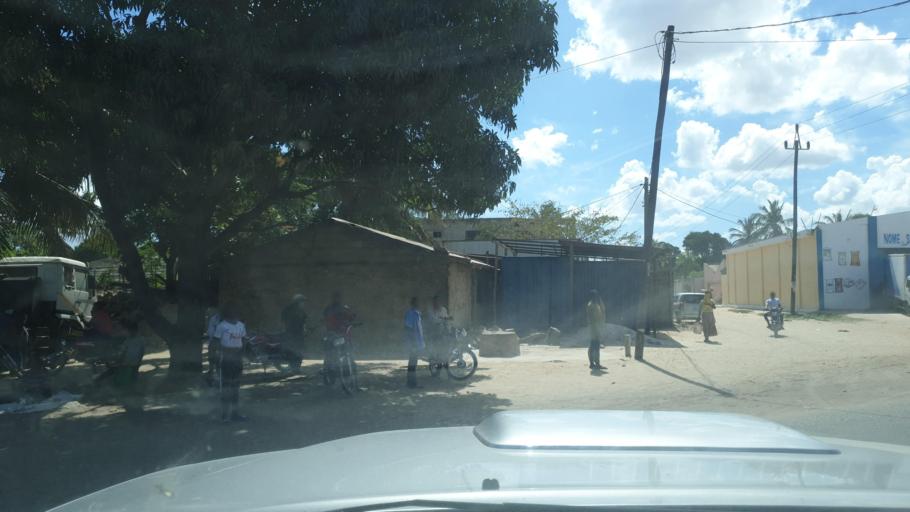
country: MZ
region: Nampula
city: Nacala
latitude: -14.5700
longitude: 40.6858
